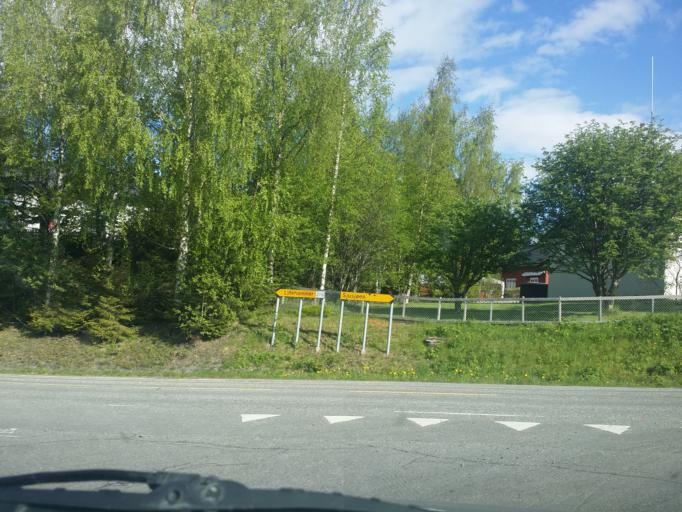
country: NO
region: Hedmark
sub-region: Ringsaker
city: Moelv
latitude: 61.1026
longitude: 10.6990
